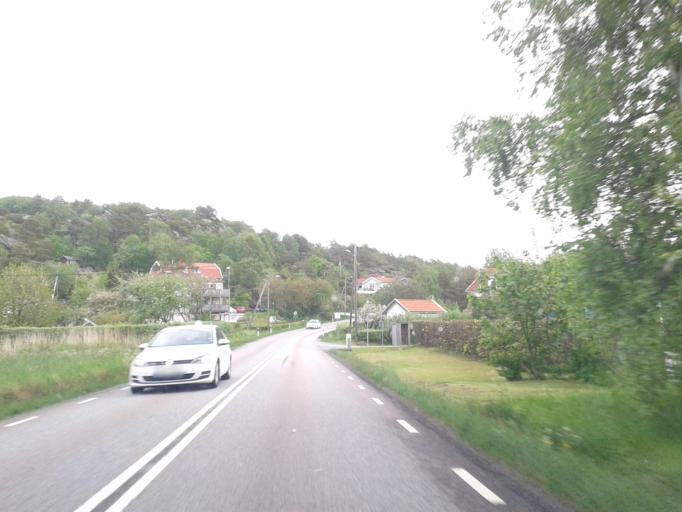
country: SE
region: Vaestra Goetaland
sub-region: Kungalvs Kommun
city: Kode
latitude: 57.8975
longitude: 11.7255
